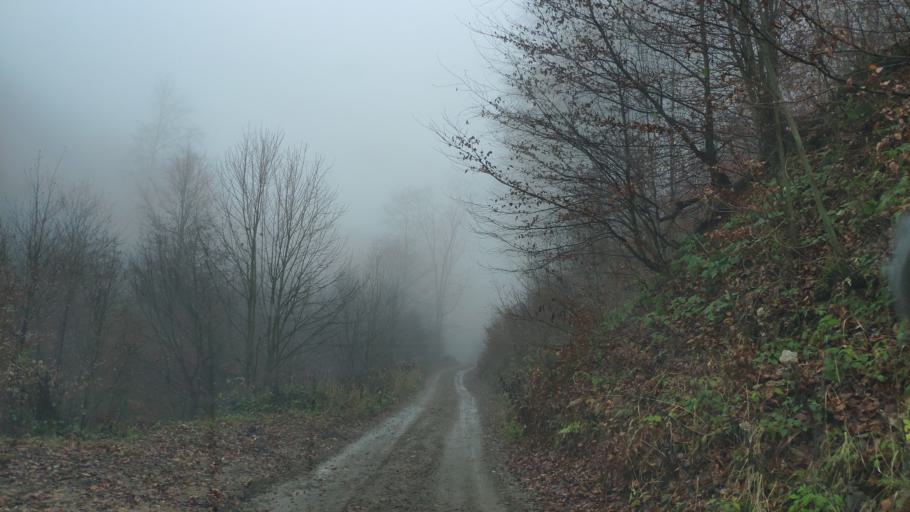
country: SK
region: Presovsky
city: Sabinov
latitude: 49.1615
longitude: 21.1949
